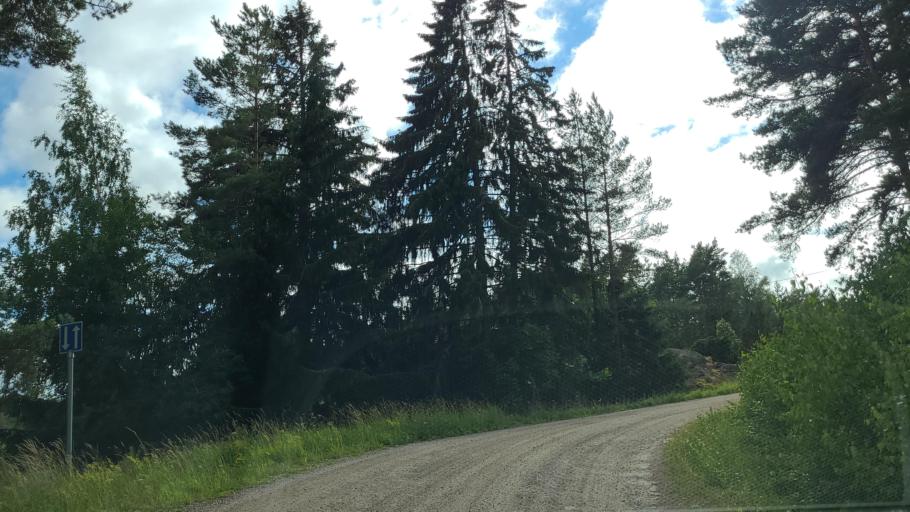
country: FI
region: Varsinais-Suomi
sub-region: Aboland-Turunmaa
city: Nagu
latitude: 60.1896
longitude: 21.7604
